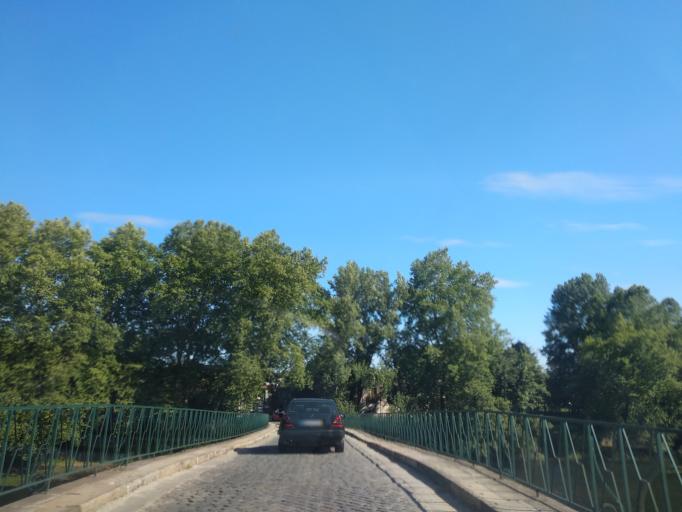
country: PT
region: Braga
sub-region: Vila Verde
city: Prado
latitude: 41.5956
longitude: -8.4629
